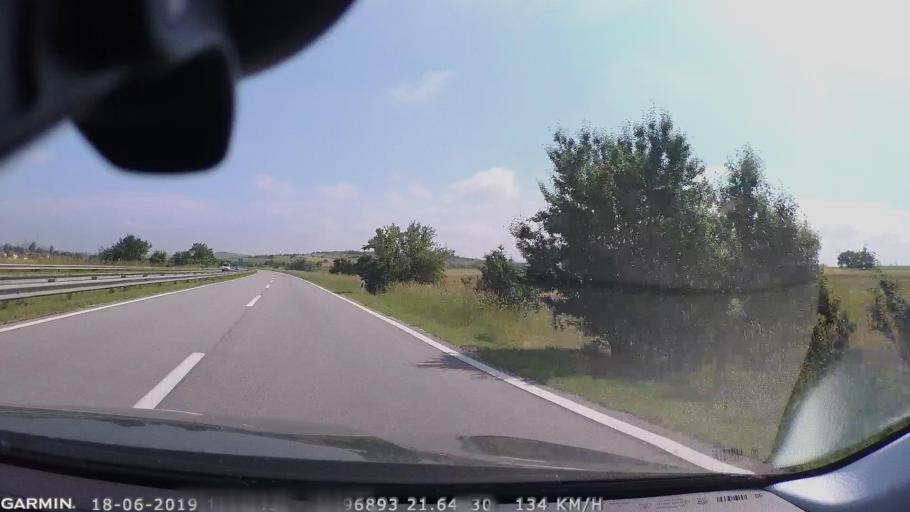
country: MK
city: Miladinovci
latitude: 41.9697
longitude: 21.6453
